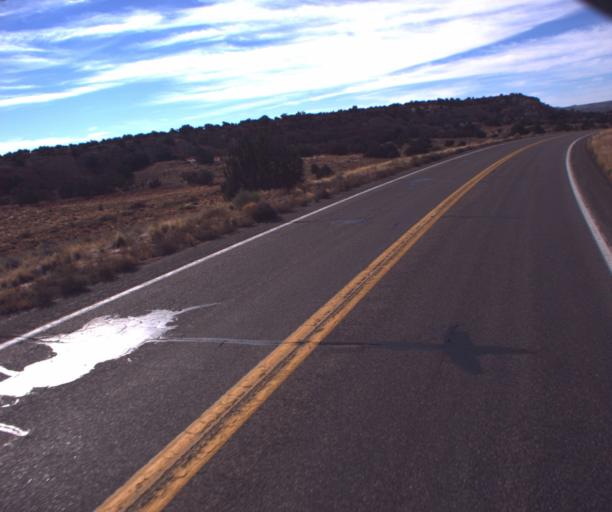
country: US
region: Arizona
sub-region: Coconino County
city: Kaibito
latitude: 36.6805
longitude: -111.2545
